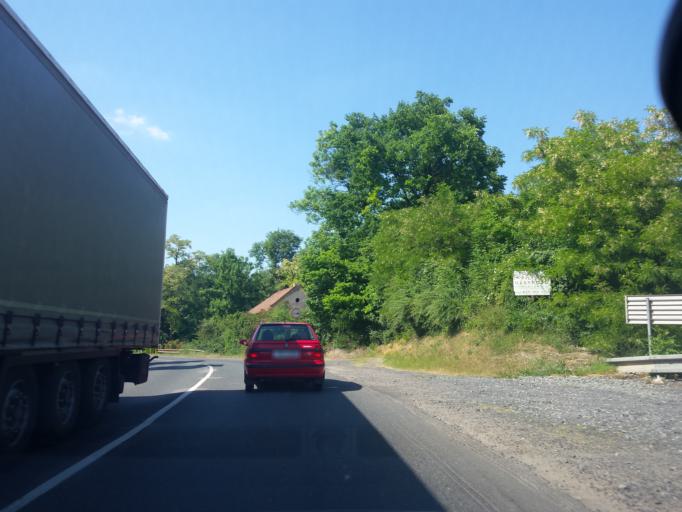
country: CZ
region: Central Bohemia
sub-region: Okres Melnik
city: Veltrusy
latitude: 50.3039
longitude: 14.3174
